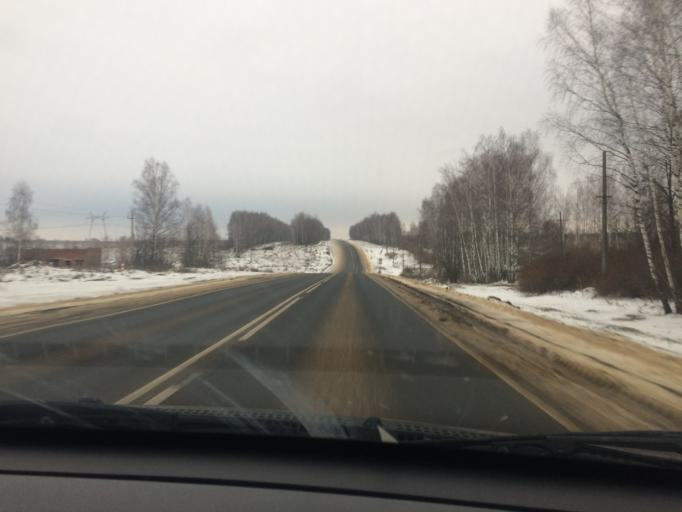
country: RU
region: Tula
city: Shvartsevskiy
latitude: 54.3215
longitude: 37.9727
